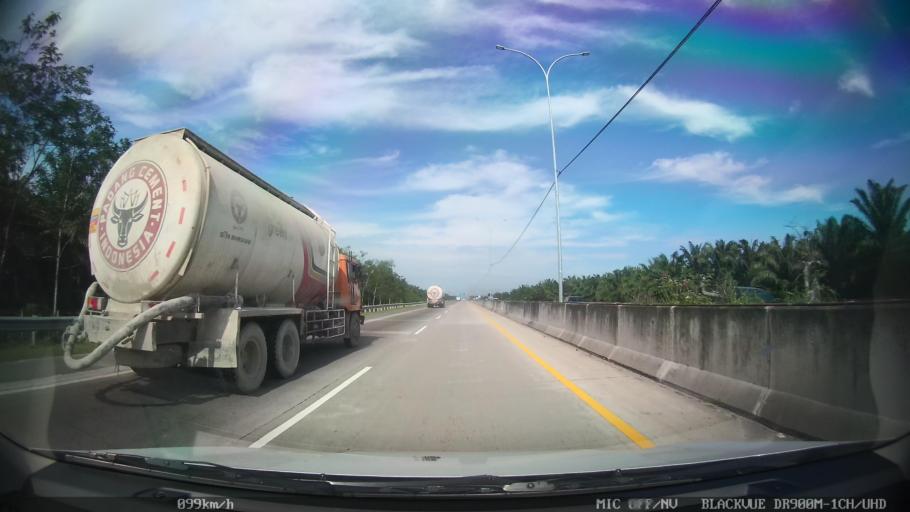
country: ID
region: North Sumatra
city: Sunggal
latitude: 3.6383
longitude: 98.6067
